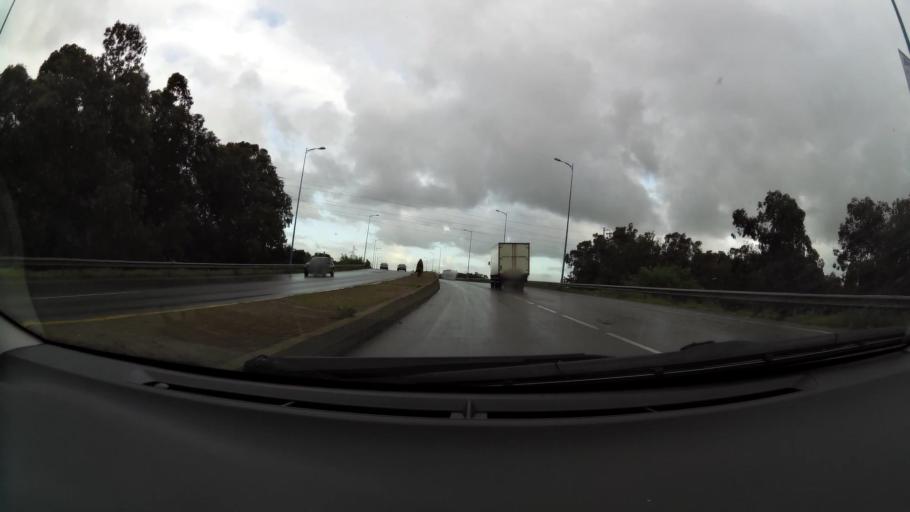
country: MA
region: Grand Casablanca
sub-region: Mohammedia
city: Mohammedia
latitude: 33.6705
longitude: -7.4068
